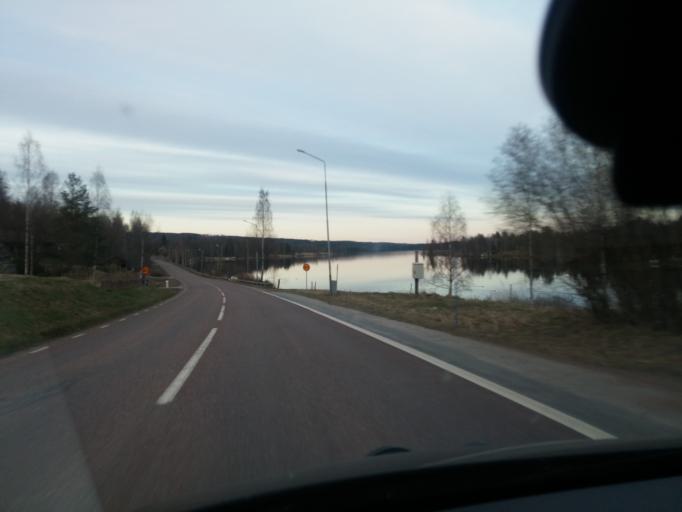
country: SE
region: Dalarna
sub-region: Faluns Kommun
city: Bjursas
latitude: 60.7120
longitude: 15.3160
